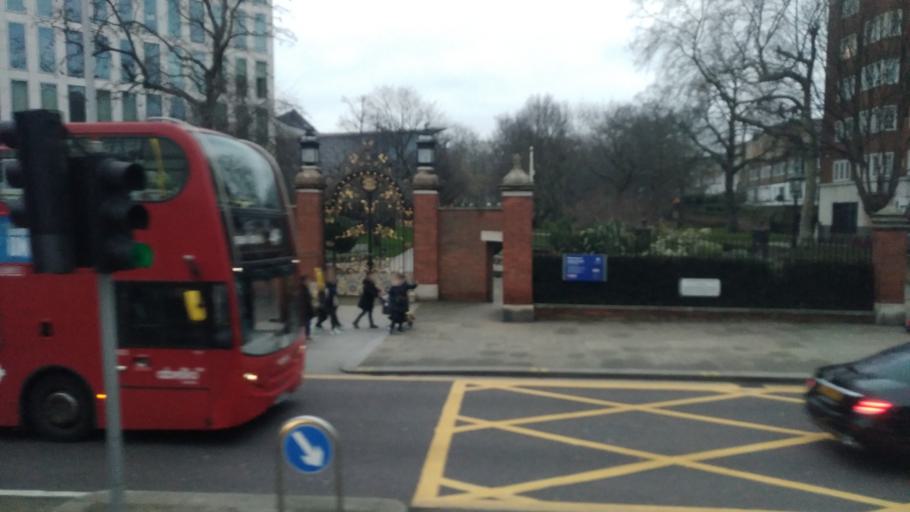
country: GB
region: England
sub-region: Greater London
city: Kensington
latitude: 51.4990
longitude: -0.1986
